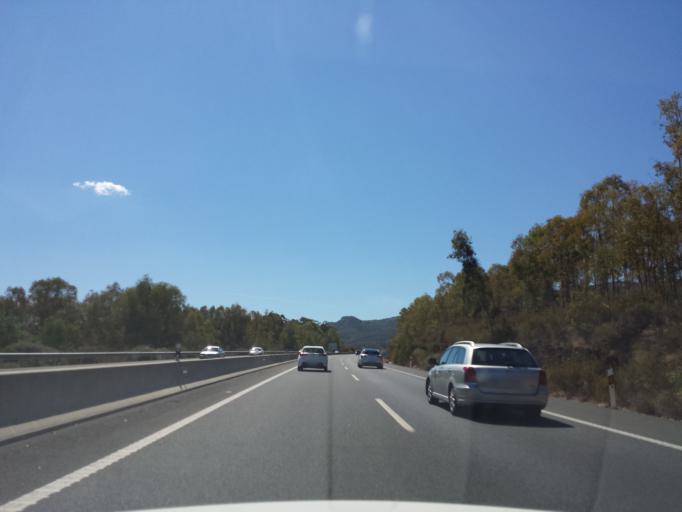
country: ES
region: Extremadura
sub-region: Provincia de Caceres
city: Romangordo
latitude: 39.7237
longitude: -5.7132
